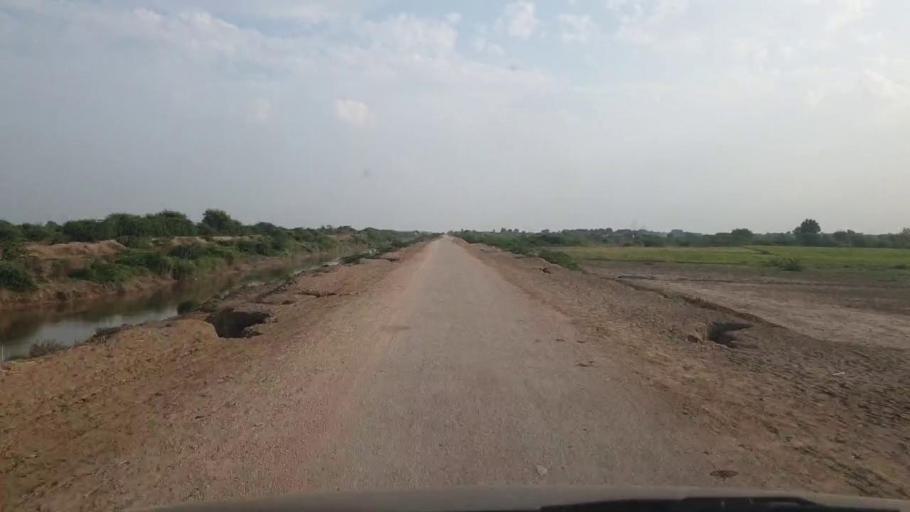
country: PK
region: Sindh
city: Badin
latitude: 24.5383
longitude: 68.6753
